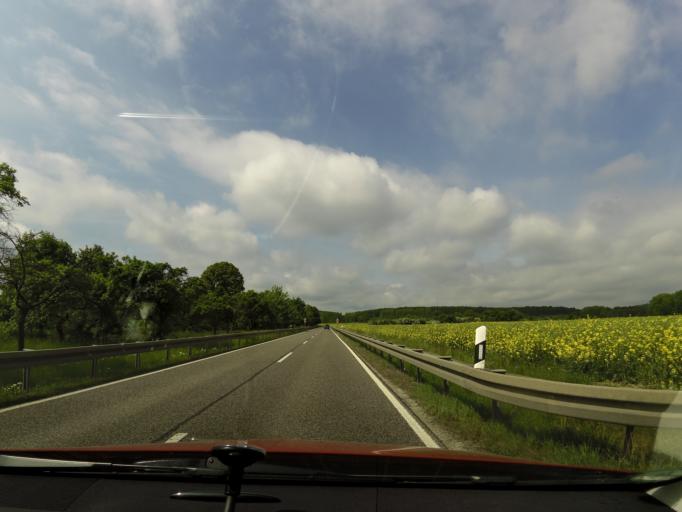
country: DE
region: Thuringia
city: Langula
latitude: 51.1455
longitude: 10.4049
